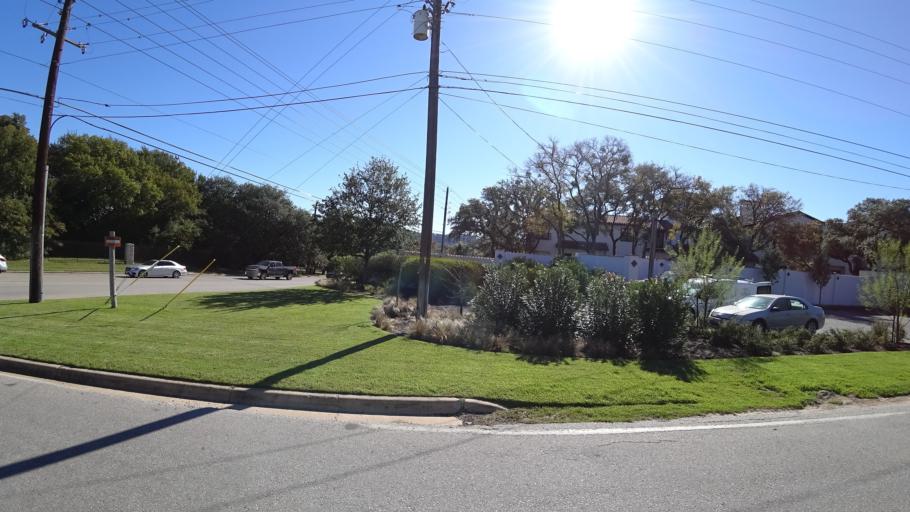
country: US
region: Texas
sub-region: Travis County
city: West Lake Hills
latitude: 30.3315
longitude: -97.7902
